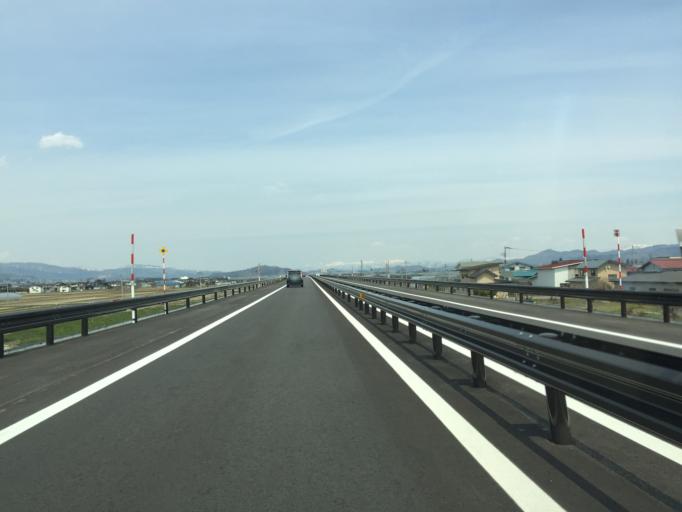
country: JP
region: Yamagata
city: Higashine
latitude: 38.4301
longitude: 140.3530
